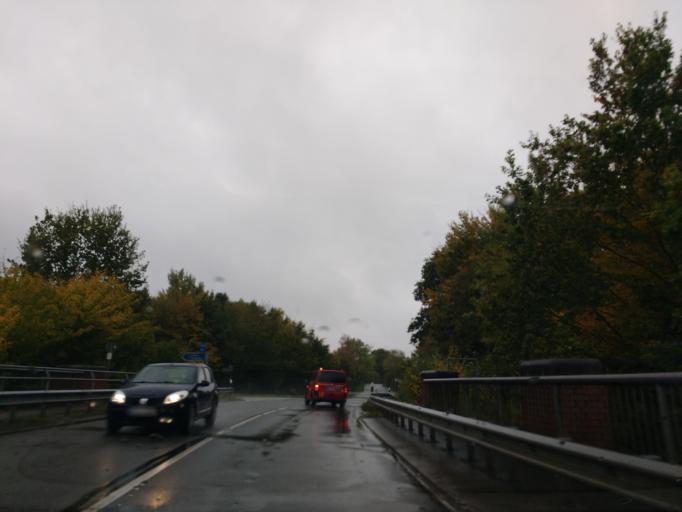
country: DE
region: Schleswig-Holstein
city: Eutin
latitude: 54.1192
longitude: 10.6383
